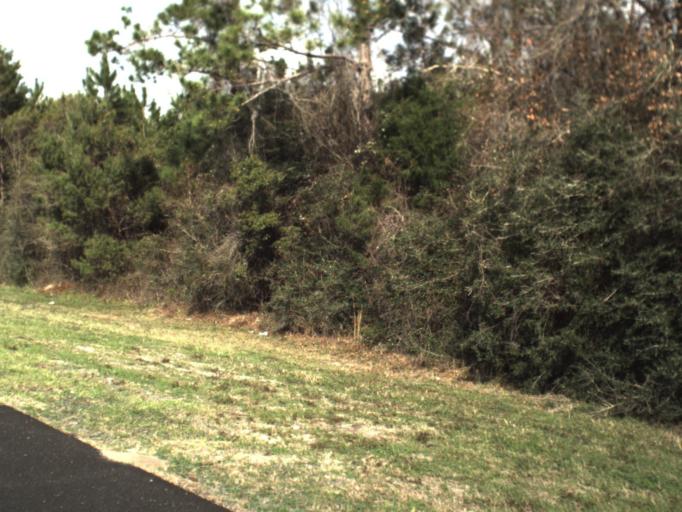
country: US
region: Florida
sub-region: Bay County
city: Youngstown
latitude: 30.3851
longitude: -85.4370
